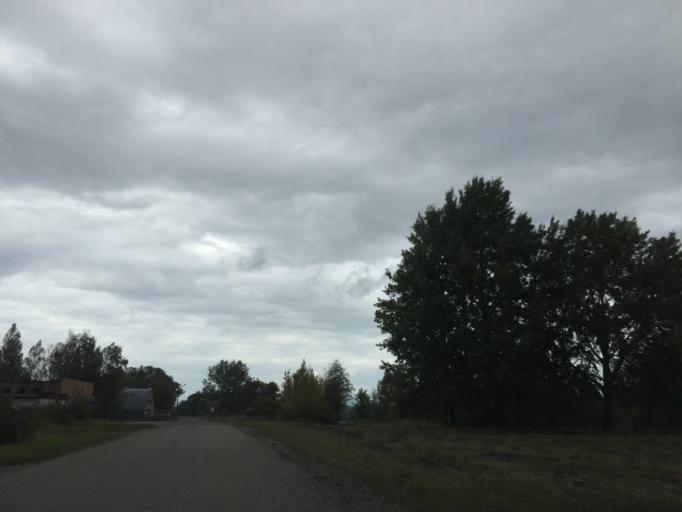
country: LV
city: Tireli
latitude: 56.7895
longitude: 23.6283
